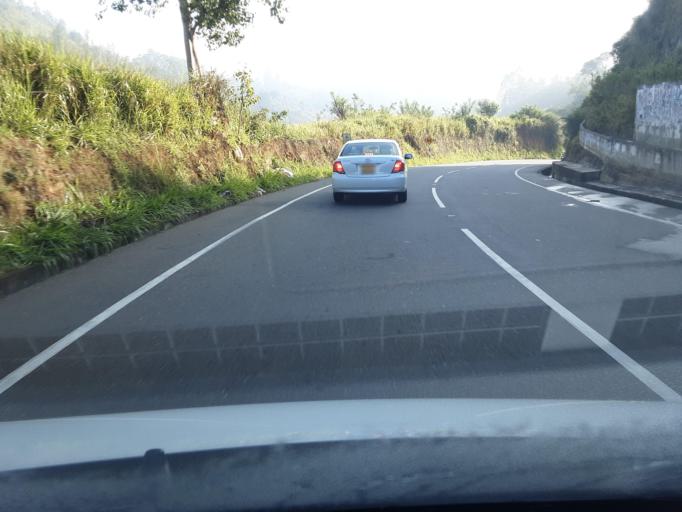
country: LK
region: Uva
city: Badulla
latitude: 6.9139
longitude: 80.9352
